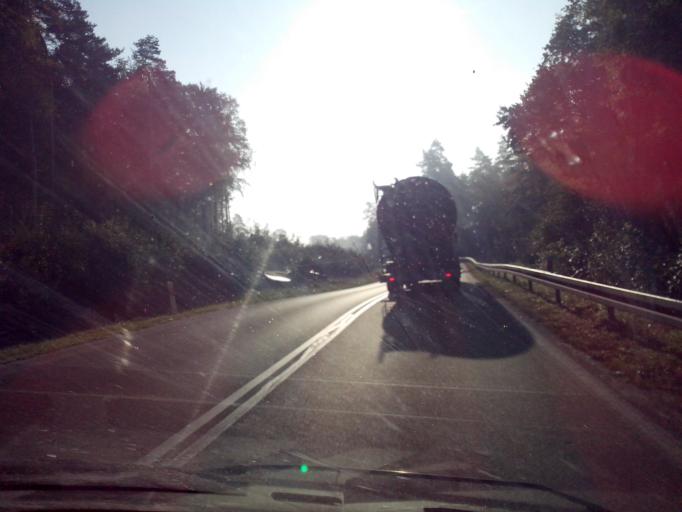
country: PL
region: Subcarpathian Voivodeship
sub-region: Powiat przemyski
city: Krasiczyn
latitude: 49.7878
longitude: 22.6152
